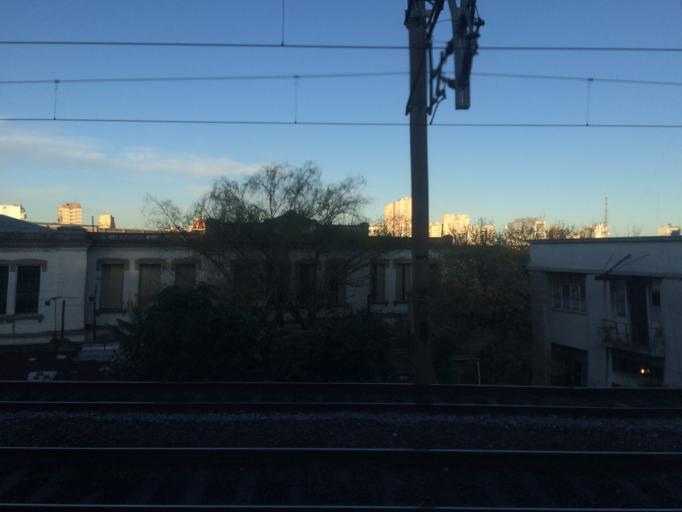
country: AR
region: Buenos Aires
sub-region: Partido de Avellaneda
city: Avellaneda
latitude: -34.6414
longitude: -58.3807
